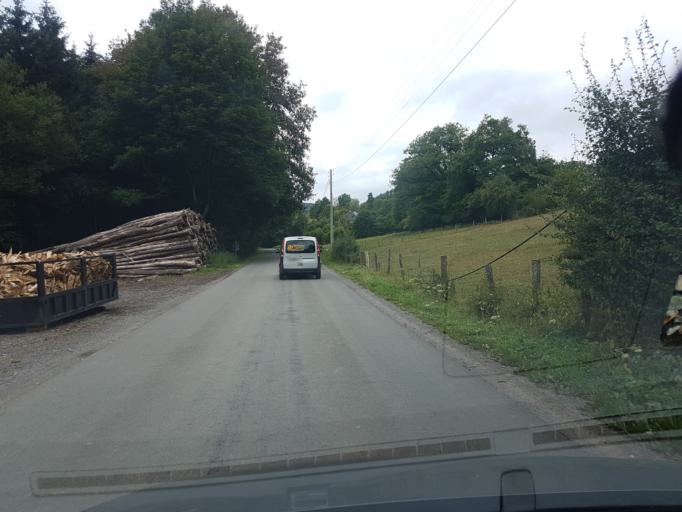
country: BE
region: Wallonia
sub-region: Province du Luxembourg
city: Manhay
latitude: 50.2648
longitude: 5.6548
